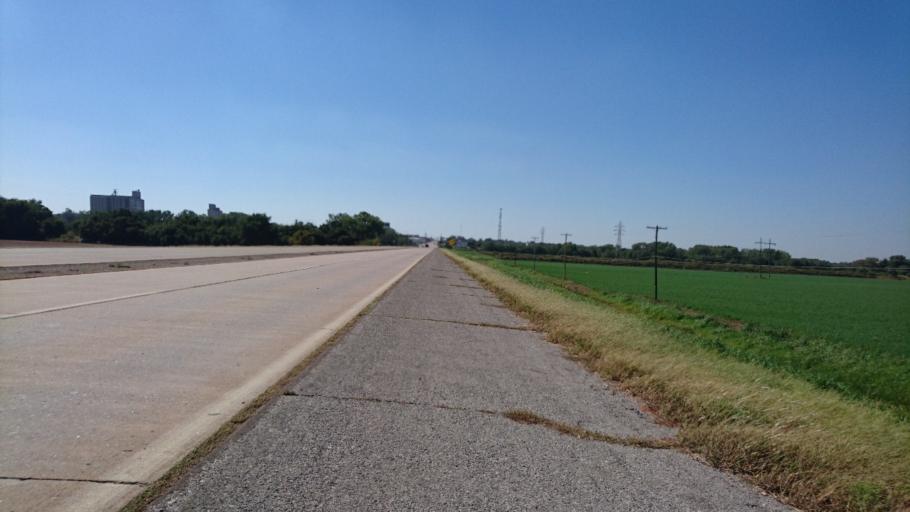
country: US
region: Oklahoma
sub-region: Custer County
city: Clinton
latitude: 35.5157
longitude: -98.9511
